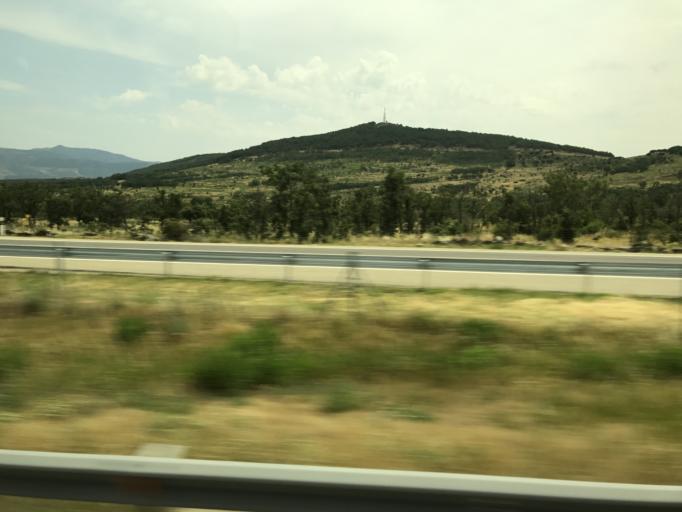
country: ES
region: Madrid
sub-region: Provincia de Madrid
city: Buitrago del Lozoya
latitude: 40.9670
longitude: -3.6411
